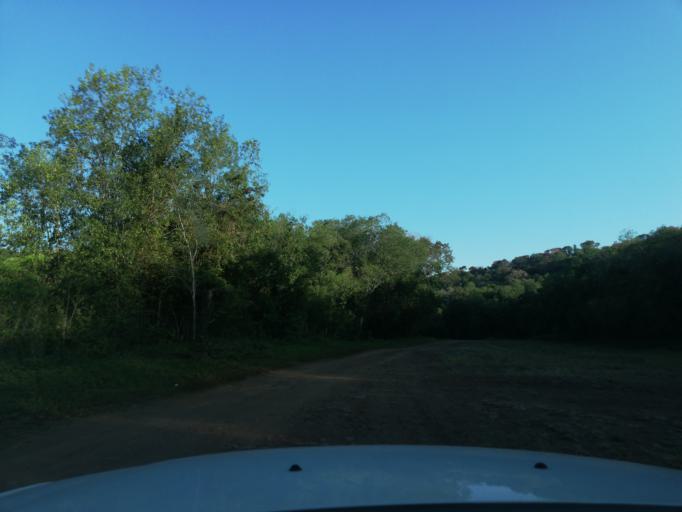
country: AR
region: Misiones
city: Cerro Cora
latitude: -27.6134
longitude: -55.7058
